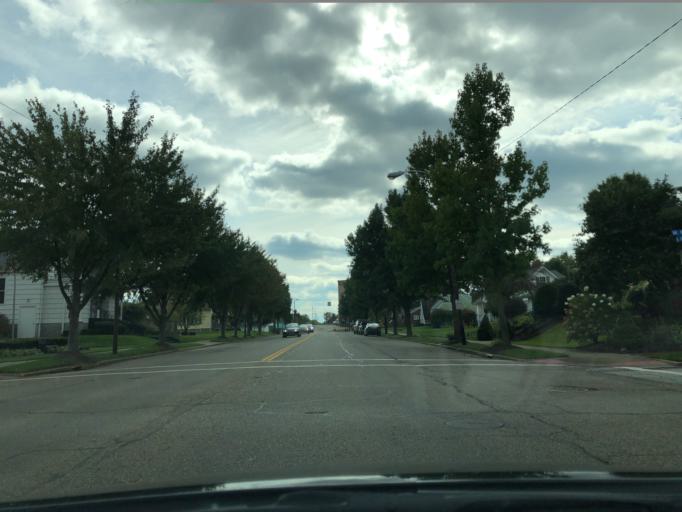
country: US
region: Ohio
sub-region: Stark County
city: Brewster
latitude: 40.7088
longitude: -81.5980
